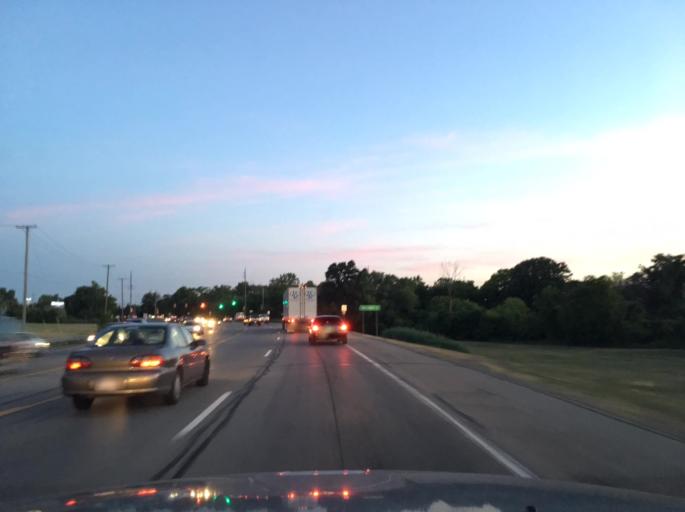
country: US
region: Michigan
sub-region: Macomb County
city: Clinton
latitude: 42.5895
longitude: -82.9024
